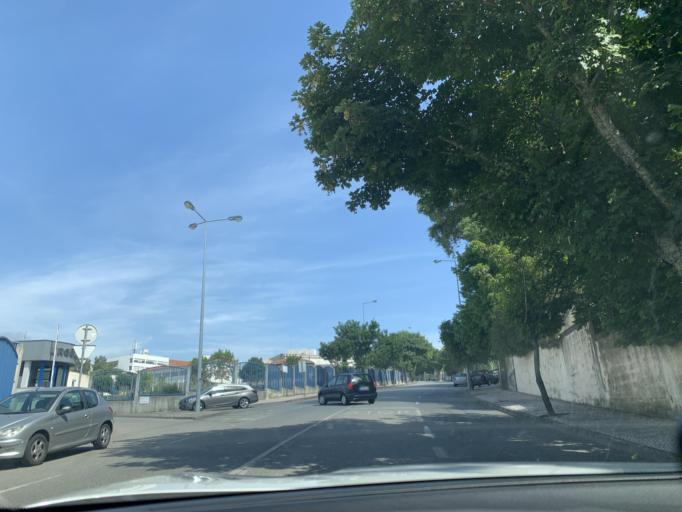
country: PT
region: Viseu
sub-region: Viseu
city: Viseu
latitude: 40.6512
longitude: -7.9042
